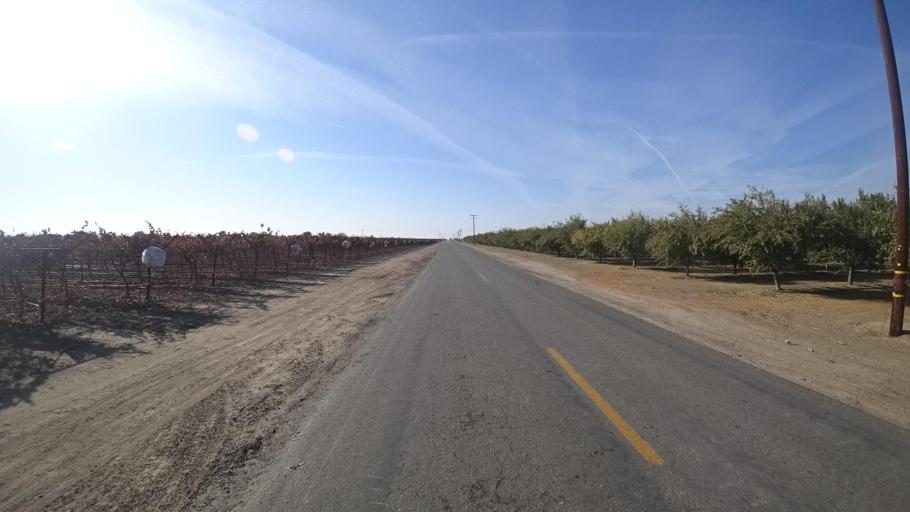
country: US
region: California
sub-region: Kern County
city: McFarland
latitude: 35.7033
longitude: -119.2728
